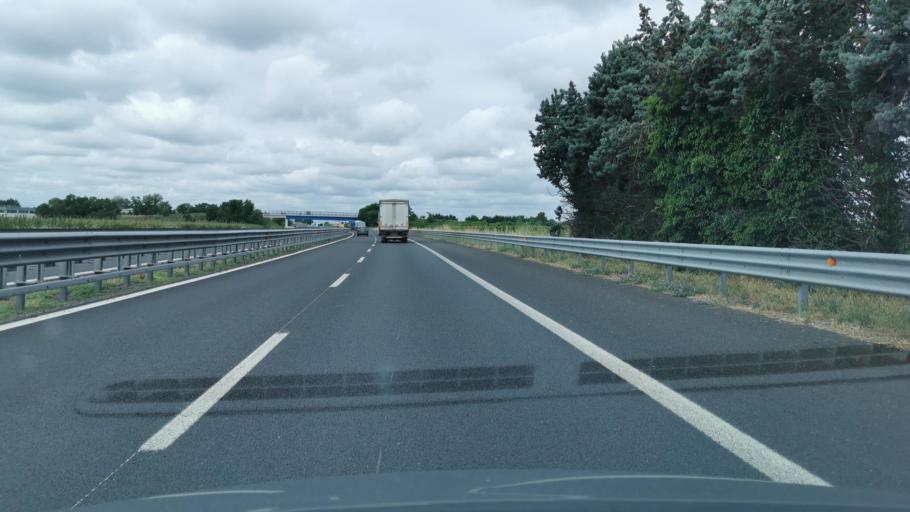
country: IT
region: Emilia-Romagna
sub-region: Provincia di Ravenna
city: Russi
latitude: 44.4076
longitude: 12.0156
